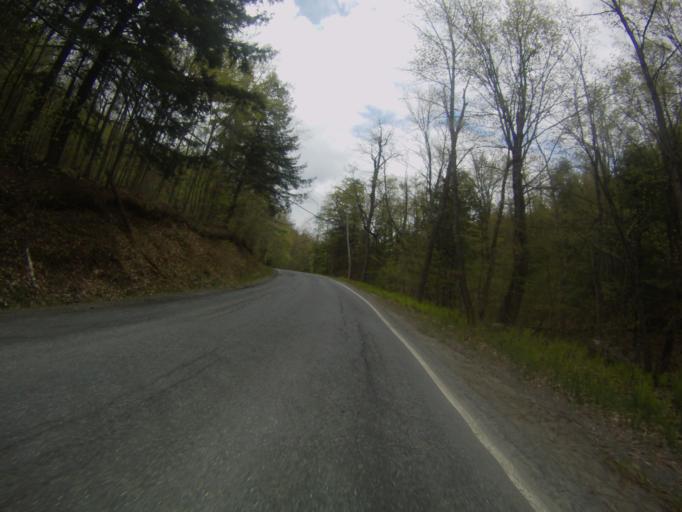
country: US
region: New York
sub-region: Essex County
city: Port Henry
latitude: 43.9814
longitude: -73.4889
